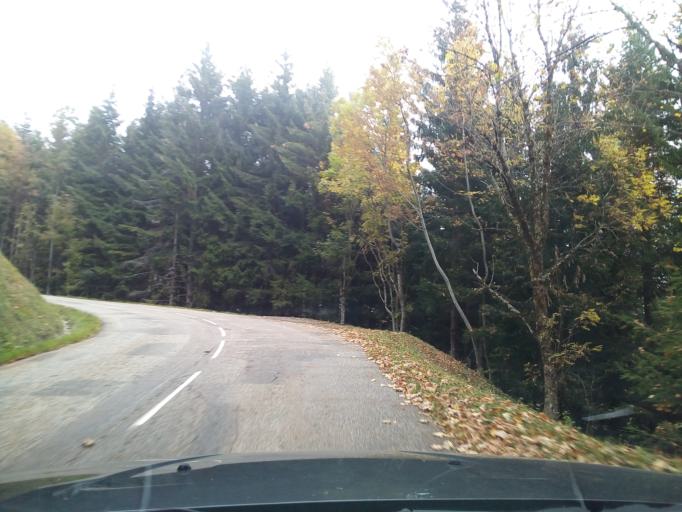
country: FR
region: Rhone-Alpes
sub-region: Departement de l'Isere
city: Bernin
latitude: 45.2947
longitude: 5.8411
